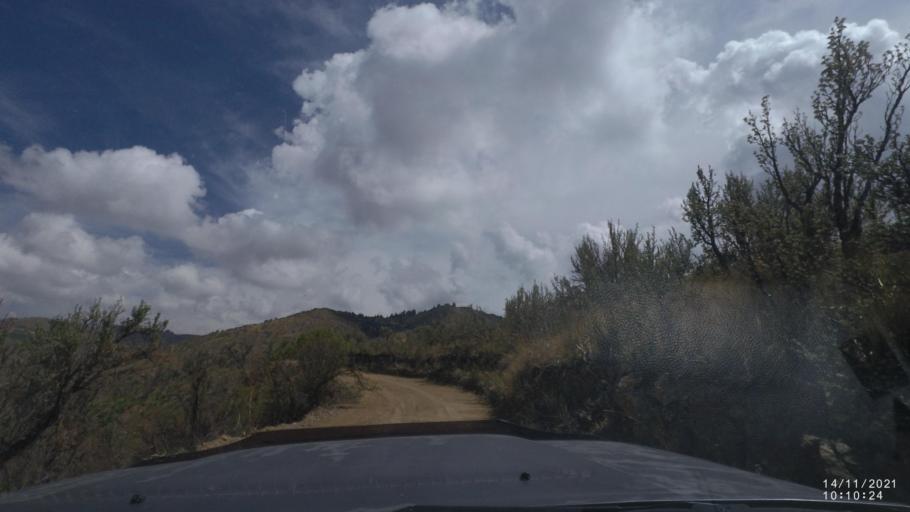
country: BO
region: Cochabamba
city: Cochabamba
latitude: -17.3486
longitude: -66.0865
